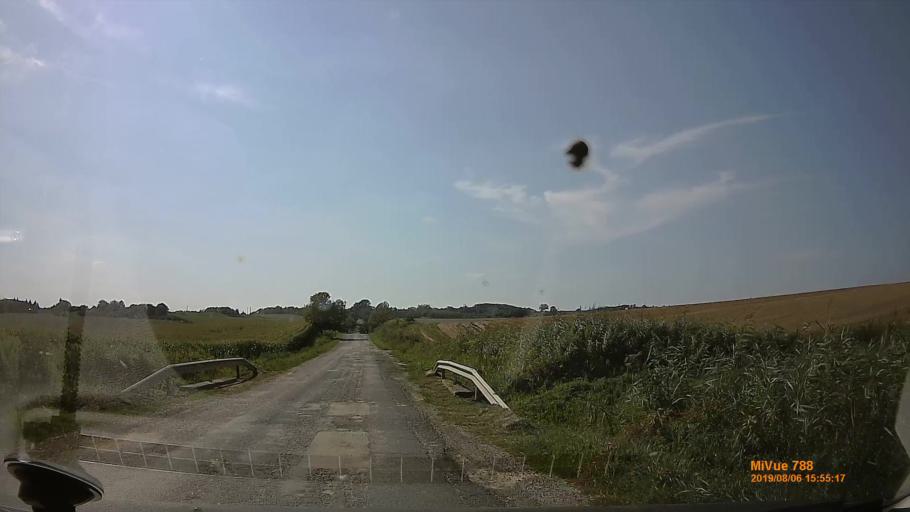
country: HU
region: Somogy
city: Csurgo
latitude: 46.2896
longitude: 17.0224
